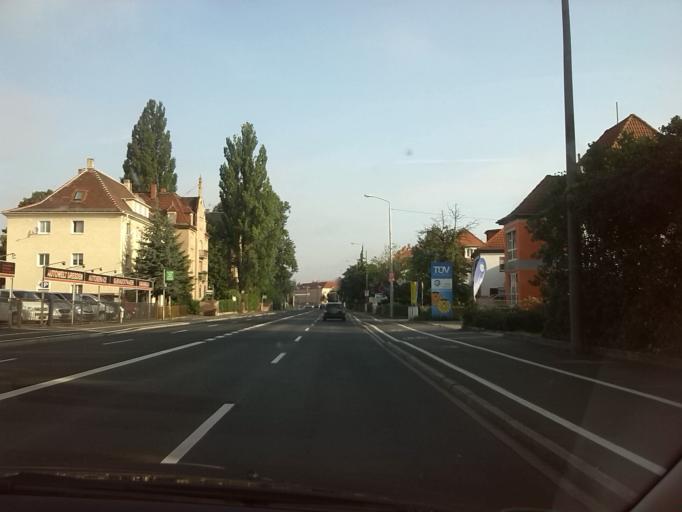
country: DE
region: Saxony
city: Dresden
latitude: 51.0176
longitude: 13.7701
